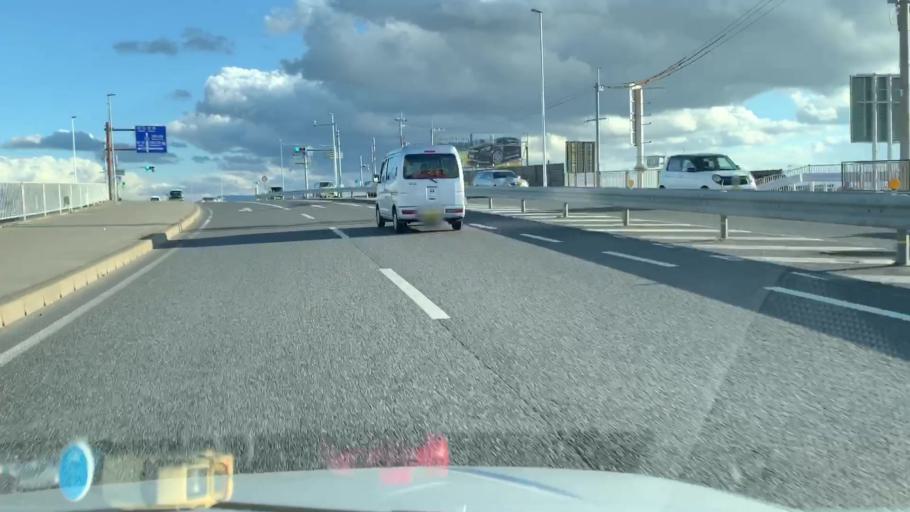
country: JP
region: Wakayama
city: Wakayama-shi
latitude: 34.2337
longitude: 135.1547
